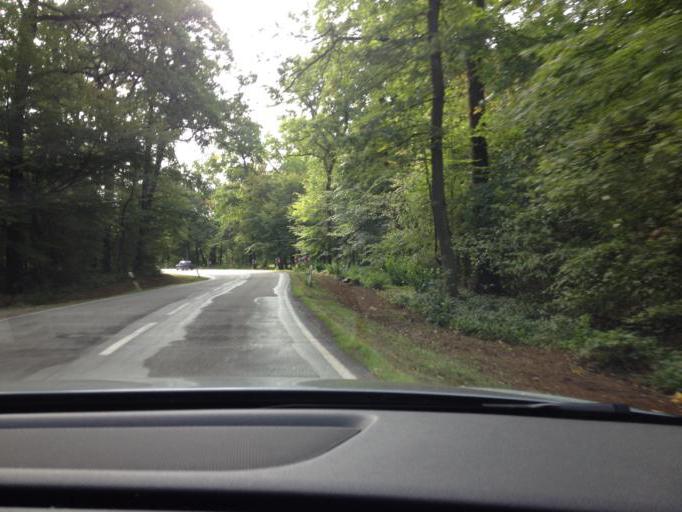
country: DE
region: Saarland
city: Mainzweiler
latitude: 49.3977
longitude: 7.1092
